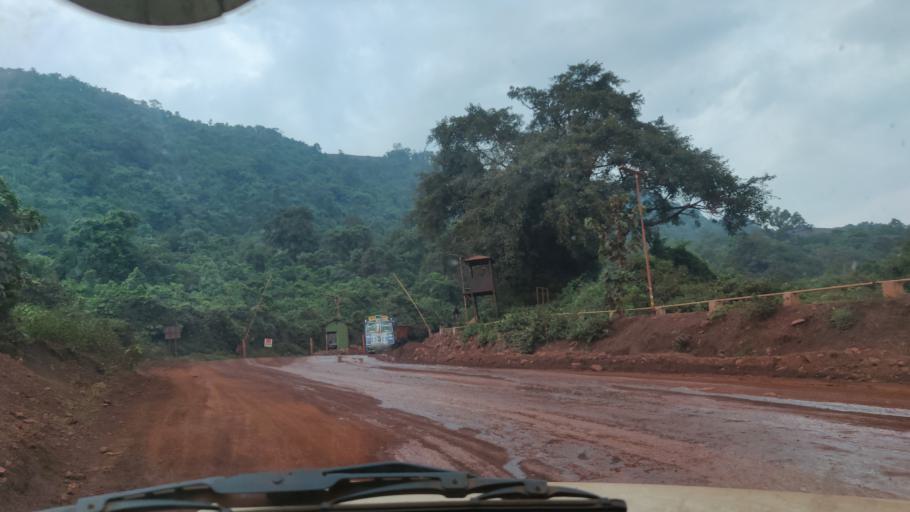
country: IN
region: Odisha
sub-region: Kendujhar
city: Barbil
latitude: 21.6239
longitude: 85.5125
